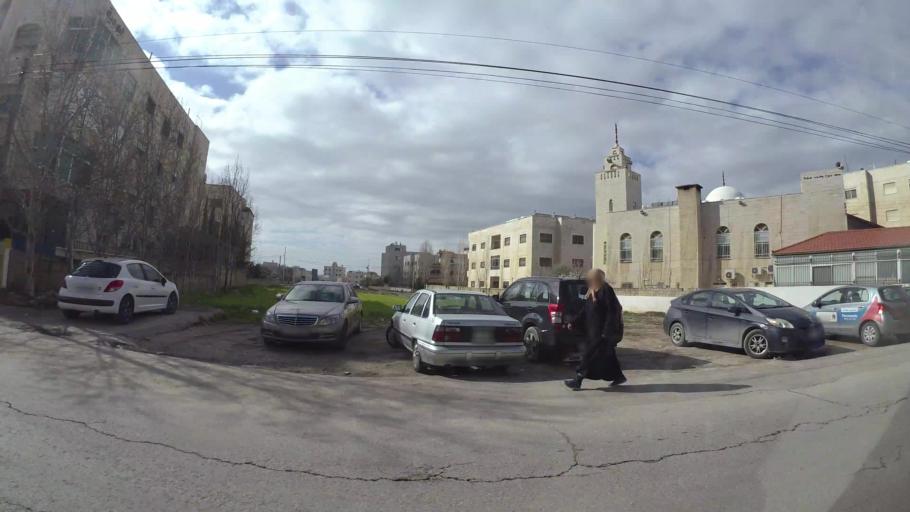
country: JO
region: Amman
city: Wadi as Sir
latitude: 31.9523
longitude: 35.8467
